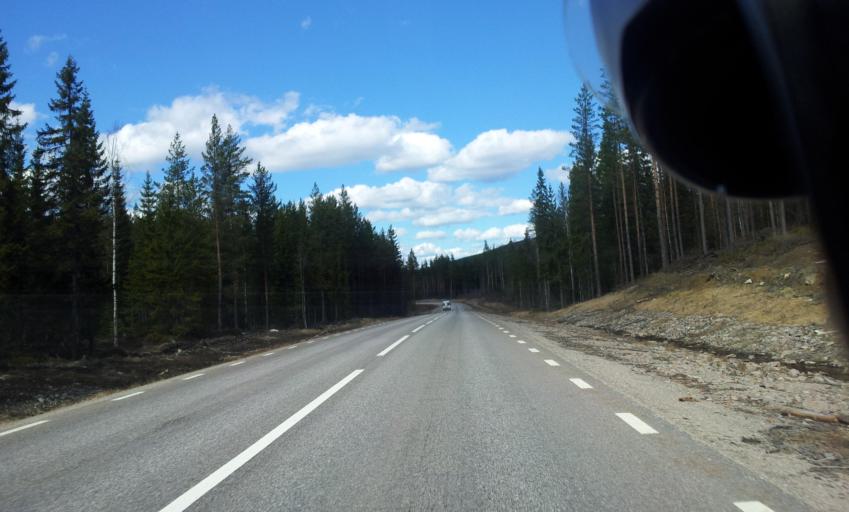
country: SE
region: Gaevleborg
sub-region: Ovanakers Kommun
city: Edsbyn
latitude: 61.1701
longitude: 15.8834
